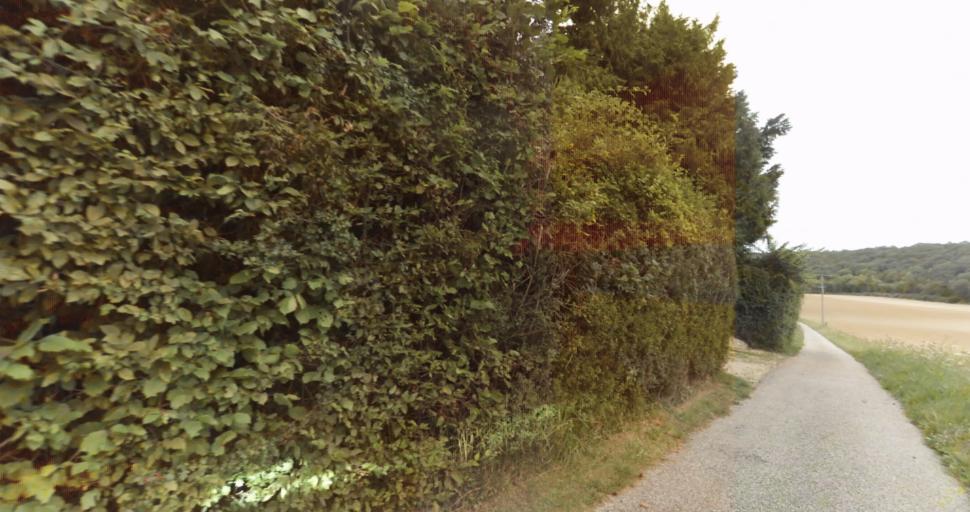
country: FR
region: Haute-Normandie
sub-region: Departement de l'Eure
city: Croth
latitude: 48.8761
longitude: 1.3636
